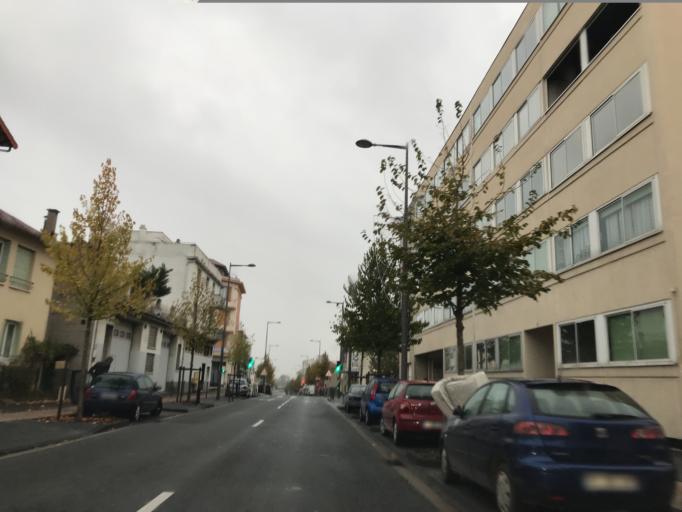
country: FR
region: Auvergne
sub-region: Departement du Puy-de-Dome
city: Clermont-Ferrand
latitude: 45.7785
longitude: 3.1102
